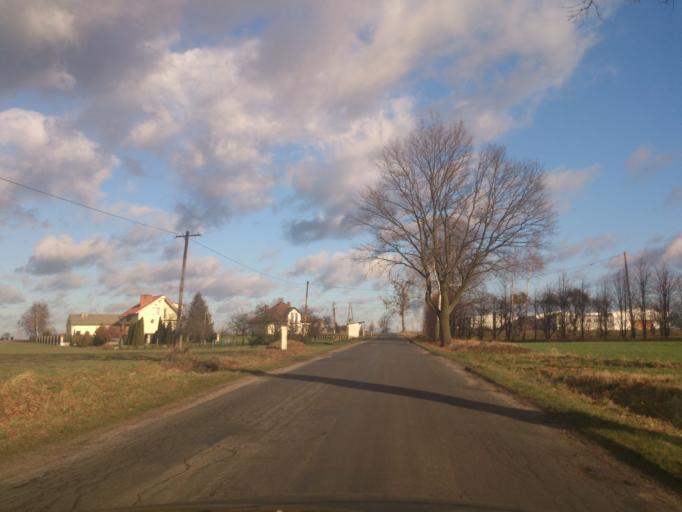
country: PL
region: Kujawsko-Pomorskie
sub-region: Powiat golubsko-dobrzynski
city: Ciechocin
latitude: 53.0512
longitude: 18.9129
